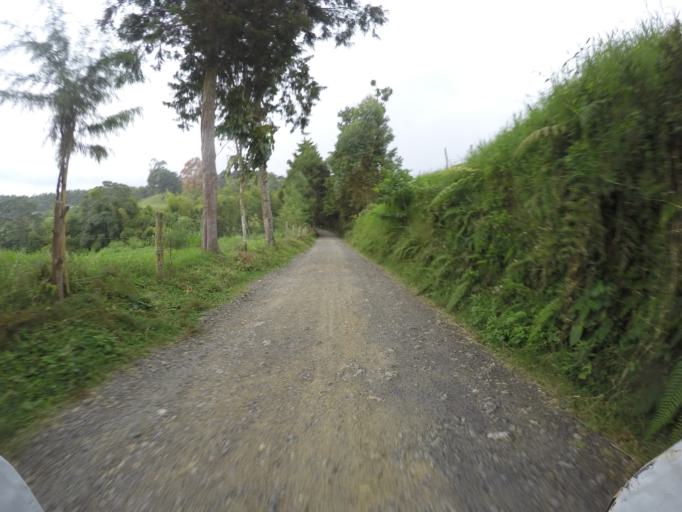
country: CO
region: Quindio
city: Filandia
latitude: 4.7121
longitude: -75.6413
